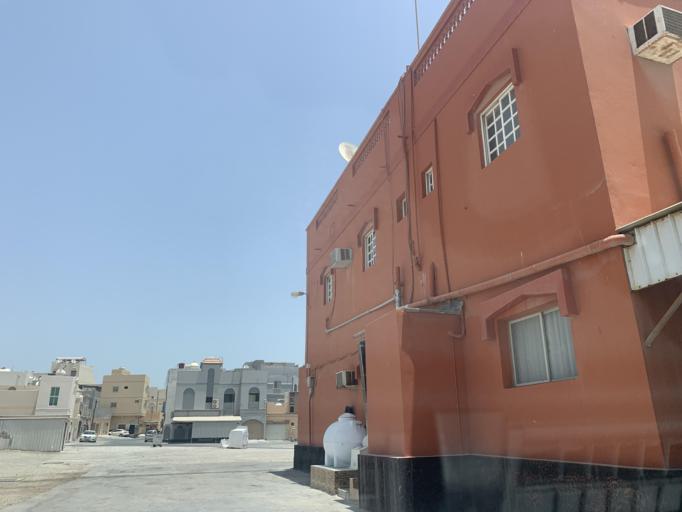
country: BH
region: Northern
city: Sitrah
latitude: 26.1626
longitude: 50.6247
